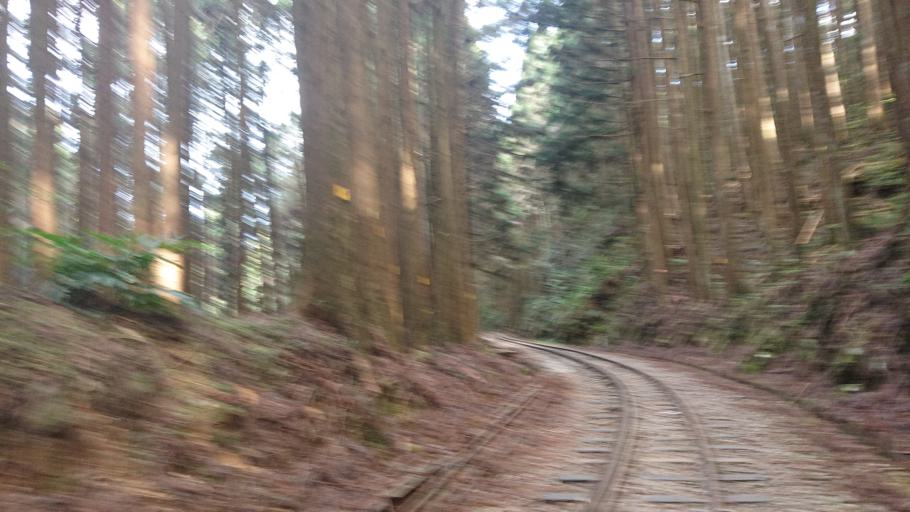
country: TW
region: Taiwan
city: Lugu
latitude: 23.5103
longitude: 120.7914
